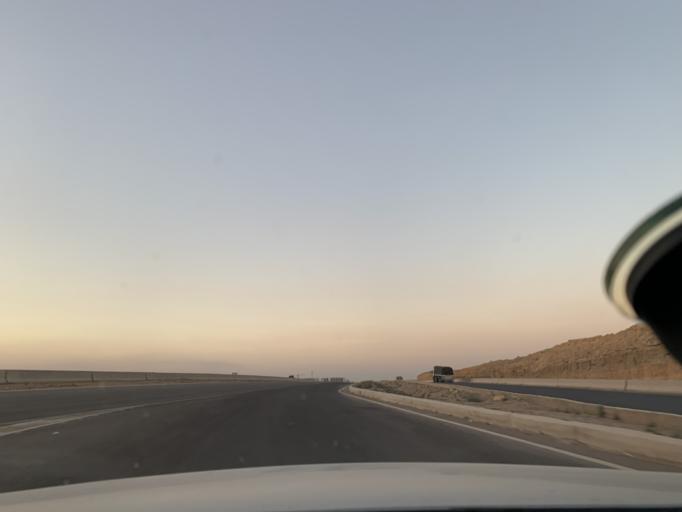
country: EG
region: Muhafazat al Qahirah
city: Halwan
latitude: 29.9523
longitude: 31.5397
